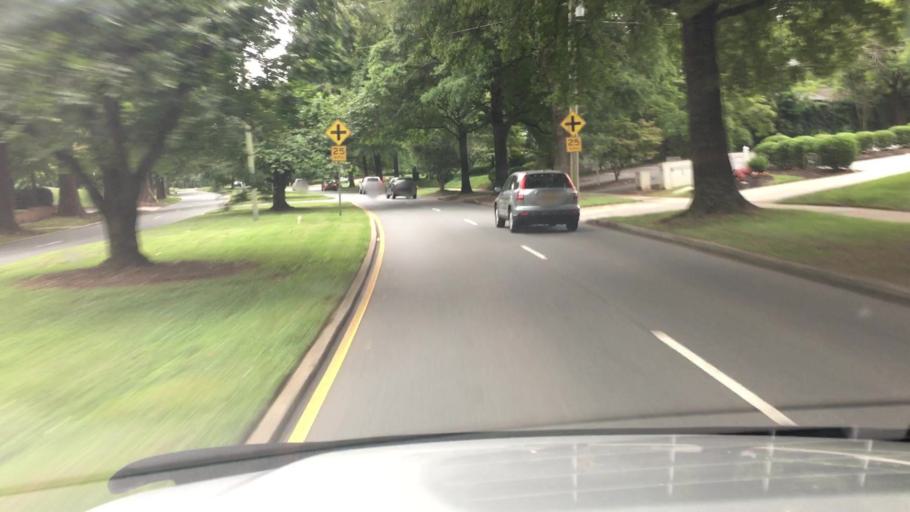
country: US
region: North Carolina
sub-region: Mecklenburg County
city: Charlotte
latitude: 35.2018
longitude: -80.8326
